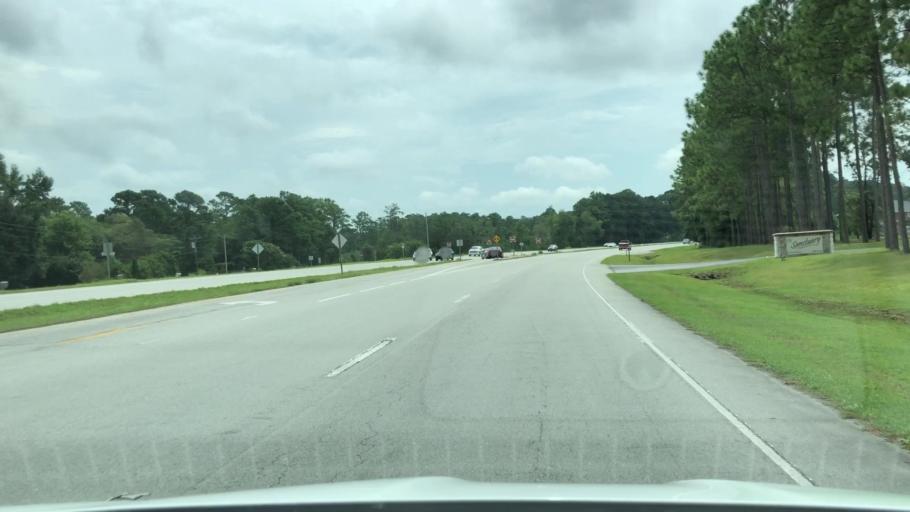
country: US
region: North Carolina
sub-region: Carteret County
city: Newport
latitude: 34.8265
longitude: -76.8765
